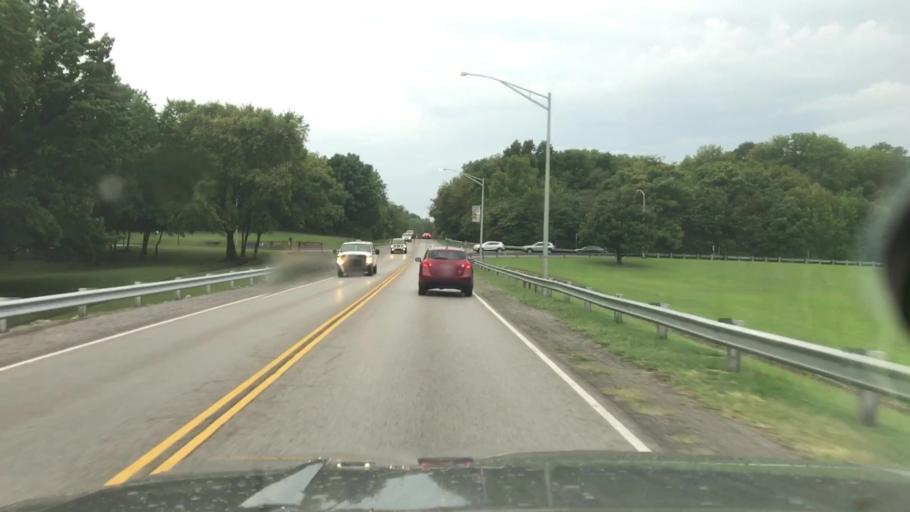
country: US
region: Tennessee
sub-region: Davidson County
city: Lakewood
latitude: 36.1542
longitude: -86.6216
